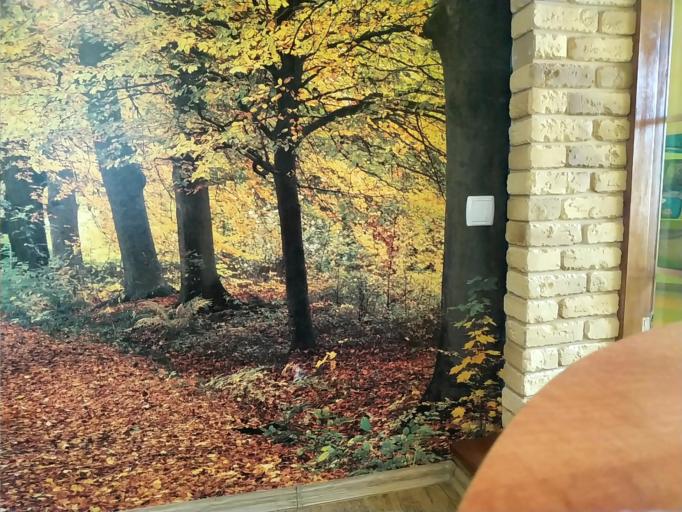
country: RU
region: Arkhangelskaya
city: Onega
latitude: 63.7321
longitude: 38.0818
